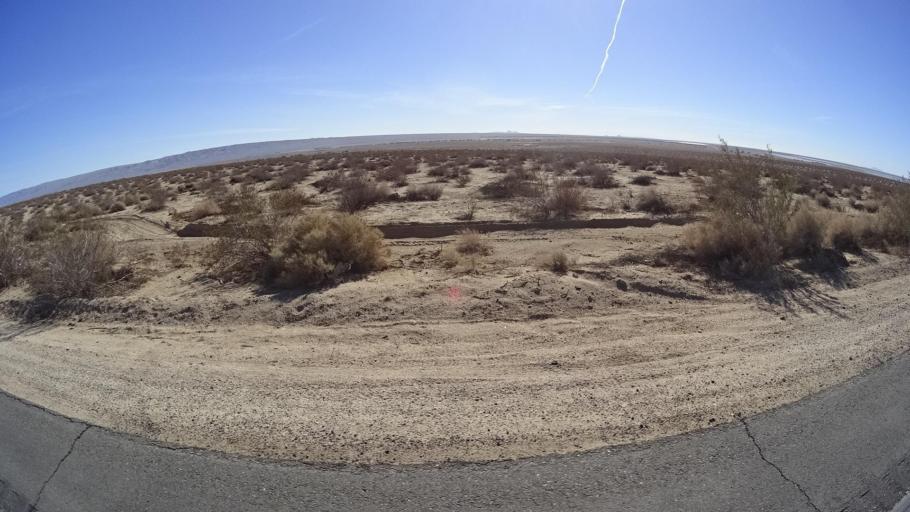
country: US
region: California
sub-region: Kern County
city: California City
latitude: 35.3156
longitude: -117.9818
